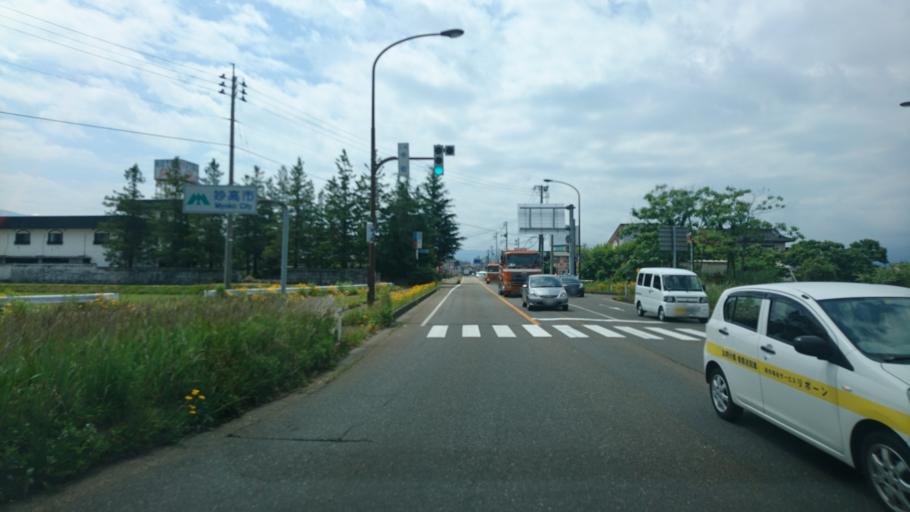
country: JP
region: Niigata
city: Arai
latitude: 37.0597
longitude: 138.2596
